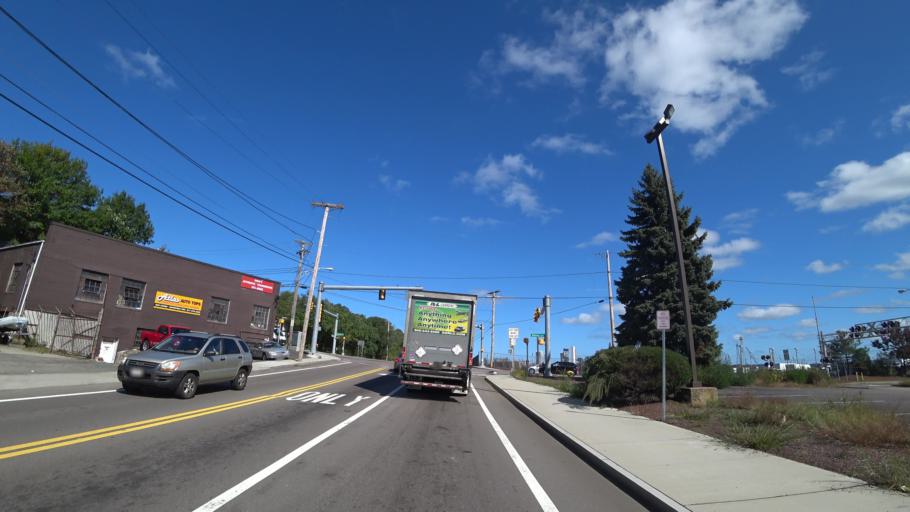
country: US
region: Massachusetts
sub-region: Norfolk County
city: Braintree
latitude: 42.2366
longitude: -70.9810
